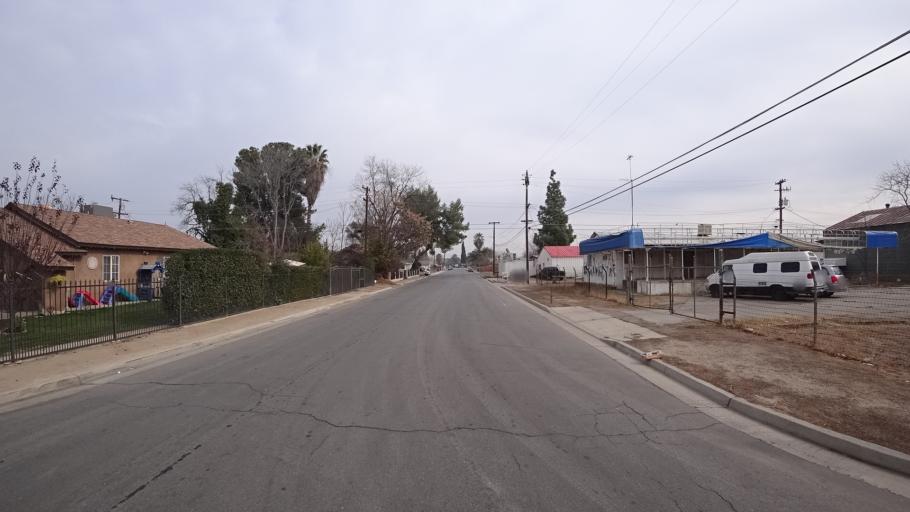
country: US
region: California
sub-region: Kern County
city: Bakersfield
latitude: 35.3617
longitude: -119.0018
